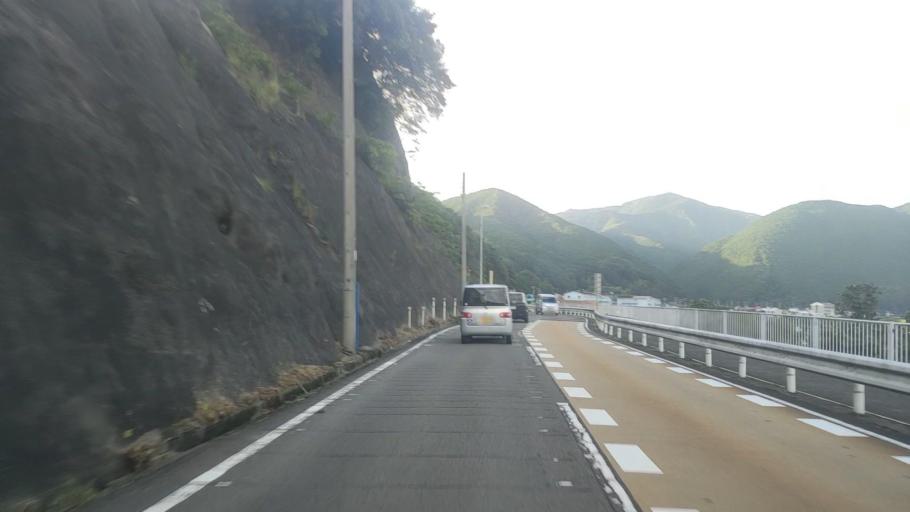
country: JP
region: Wakayama
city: Tanabe
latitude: 33.7223
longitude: 135.4812
